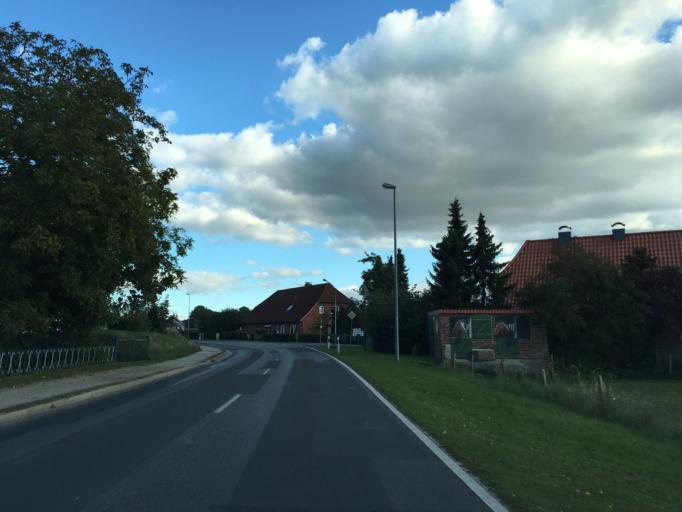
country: DE
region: Lower Saxony
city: Westergellersen
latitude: 53.2328
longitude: 10.2488
